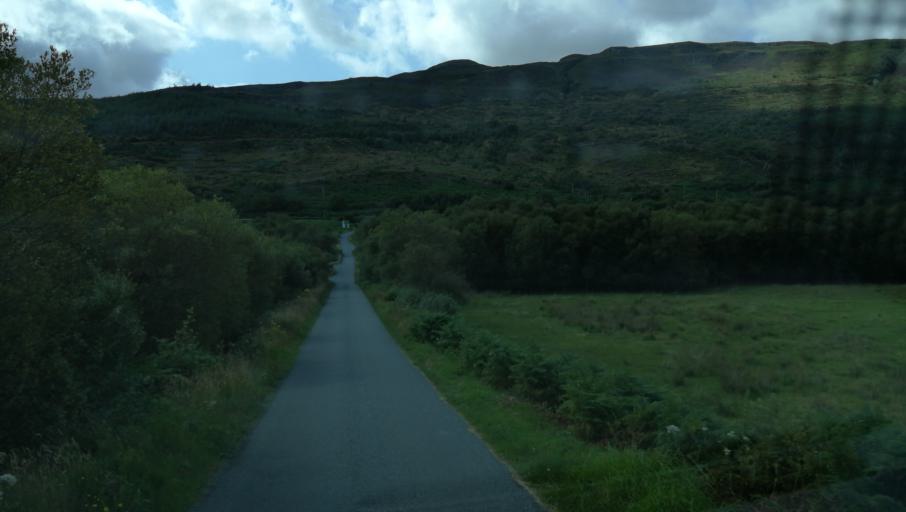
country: GB
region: Scotland
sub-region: Highland
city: Portree
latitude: 57.3872
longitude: -6.1974
